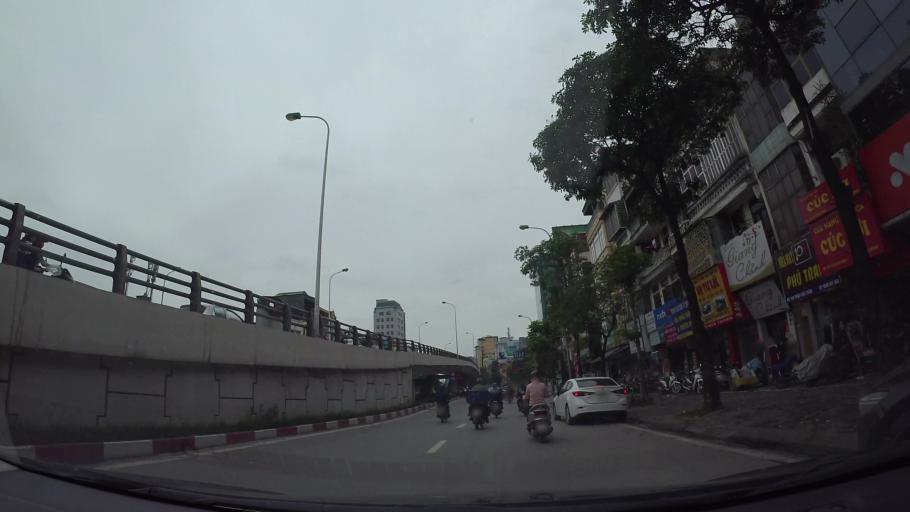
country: VN
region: Ha Noi
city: Hai BaTrung
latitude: 21.0088
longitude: 105.8526
